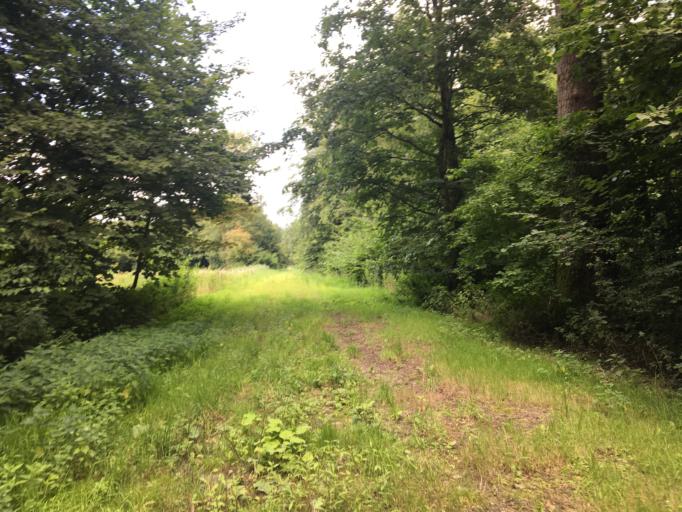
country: NL
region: Flevoland
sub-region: Gemeente Zeewolde
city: Zeewolde
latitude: 52.2824
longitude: 5.5207
